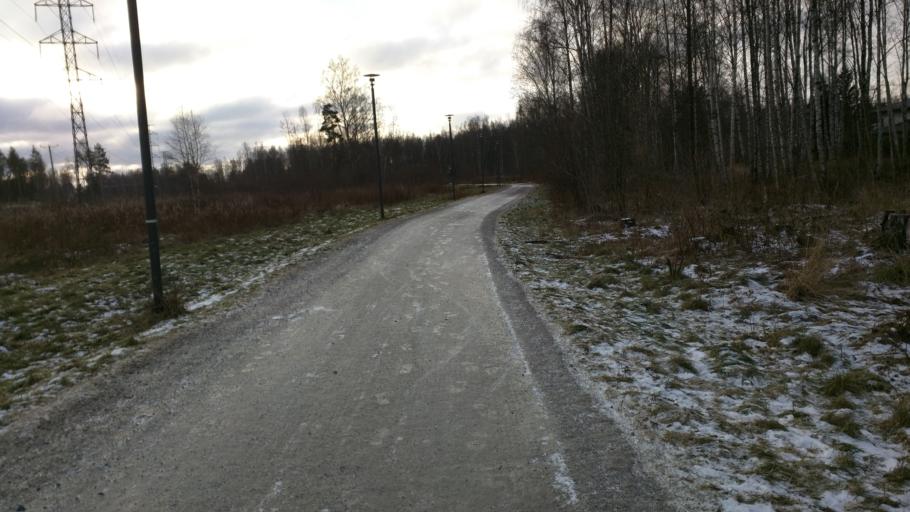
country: FI
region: Uusimaa
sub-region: Helsinki
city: Kilo
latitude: 60.2009
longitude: 24.7743
